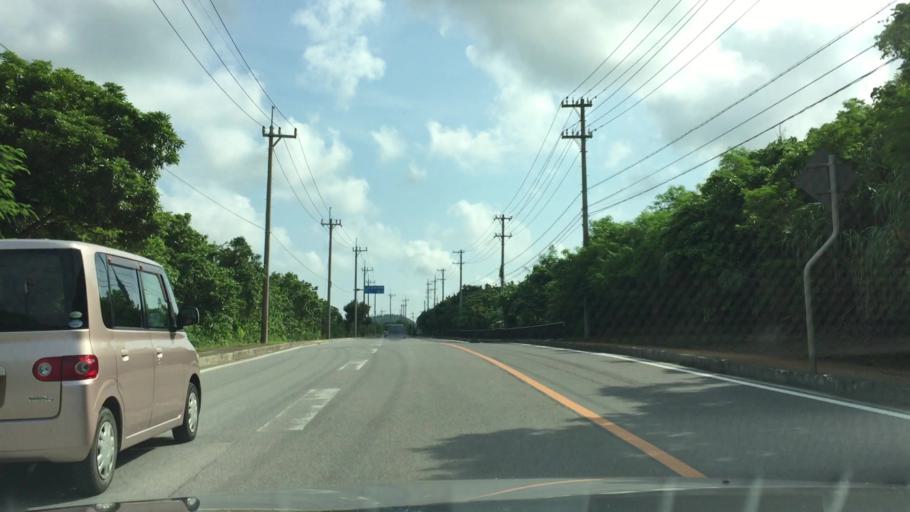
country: JP
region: Okinawa
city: Ishigaki
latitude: 24.4281
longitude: 124.2462
